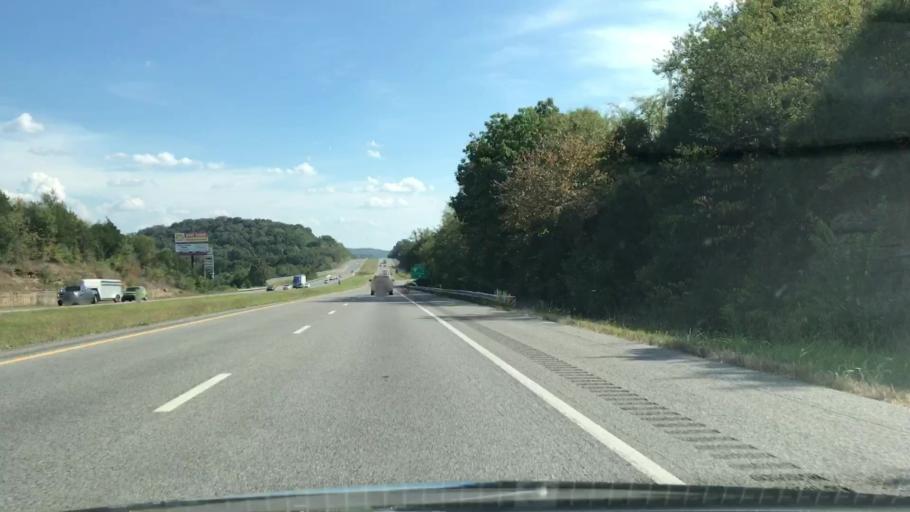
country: US
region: Alabama
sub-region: Limestone County
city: Ardmore
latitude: 35.0874
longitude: -86.8843
